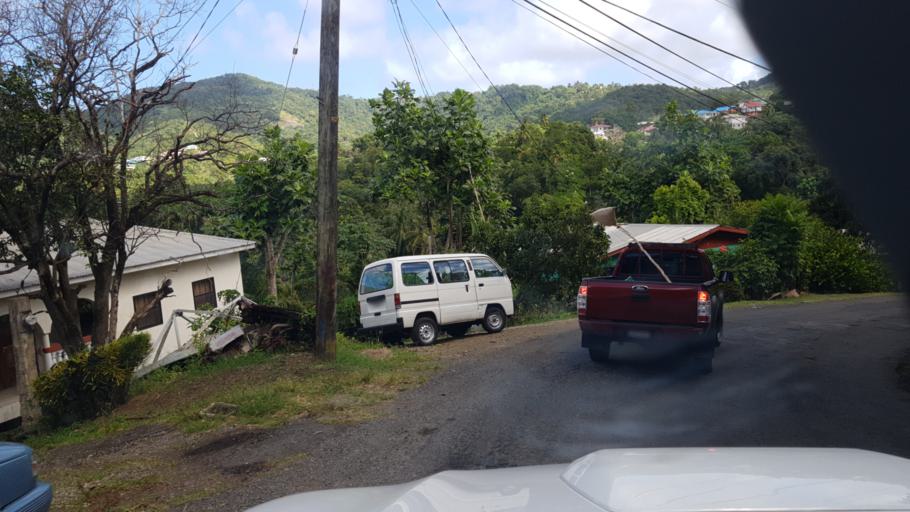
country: LC
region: Castries Quarter
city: Bisee
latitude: 14.0141
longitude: -60.9614
